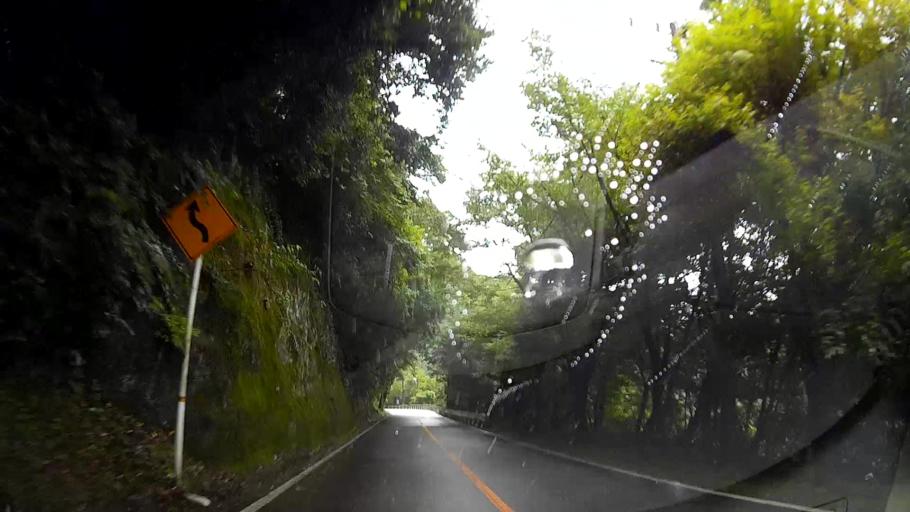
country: JP
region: Oita
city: Hita
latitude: 33.1799
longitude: 131.0055
